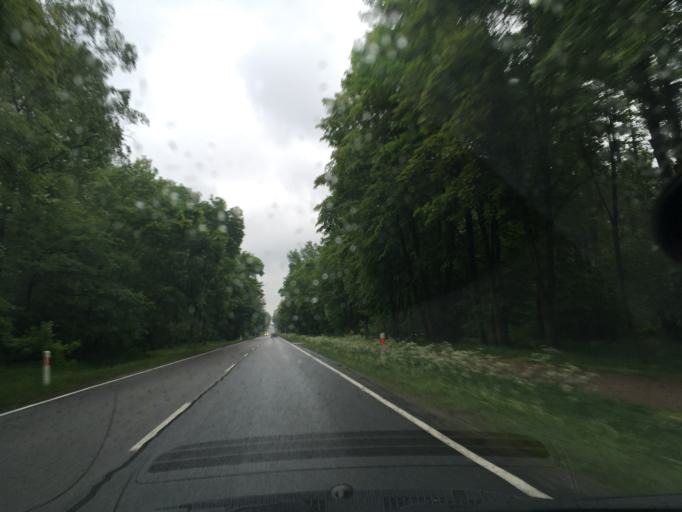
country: PL
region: Lublin Voivodeship
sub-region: Powiat rycki
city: Deblin
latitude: 51.5742
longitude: 21.8980
